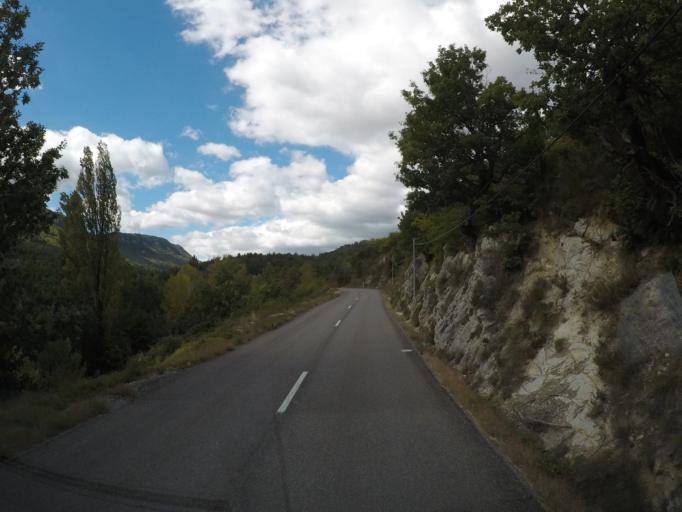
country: FR
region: Provence-Alpes-Cote d'Azur
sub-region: Departement des Hautes-Alpes
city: Laragne-Monteglin
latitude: 44.1749
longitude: 5.7027
